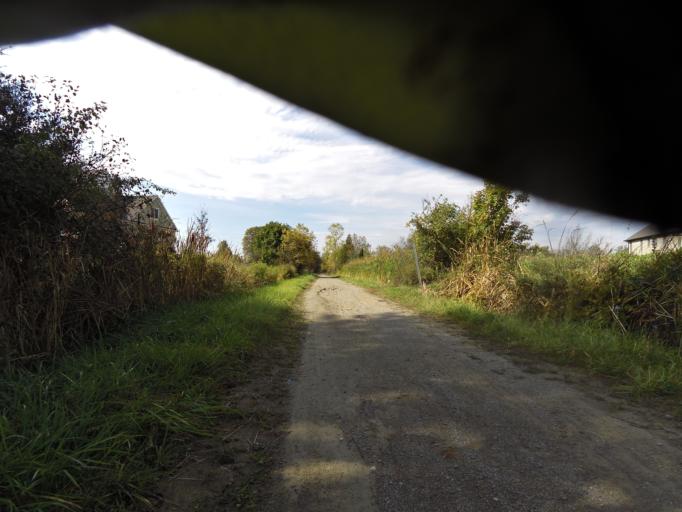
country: CA
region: Ontario
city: Brantford
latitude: 43.1801
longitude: -80.1692
